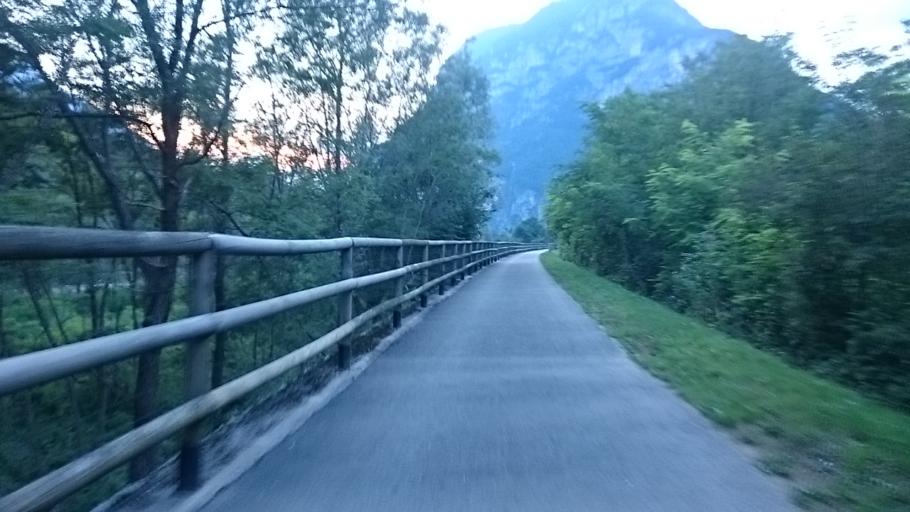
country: IT
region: Trentino-Alto Adige
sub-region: Provincia di Trento
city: Grigno
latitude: 46.0064
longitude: 11.6415
